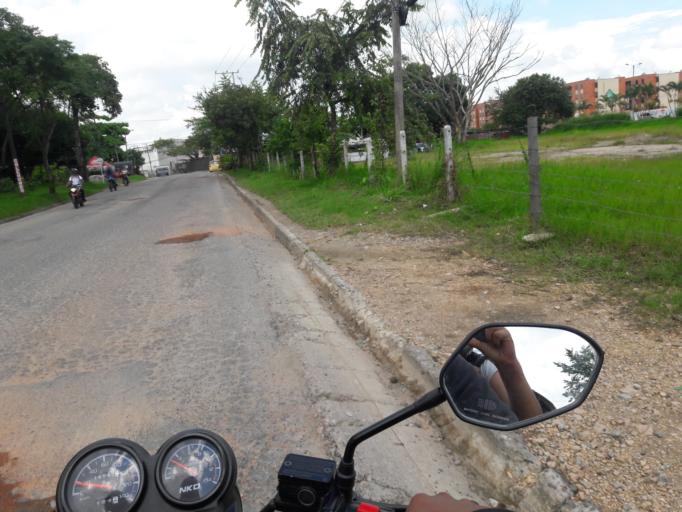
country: CO
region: Tolima
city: Ibague
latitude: 4.4468
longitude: -75.1621
